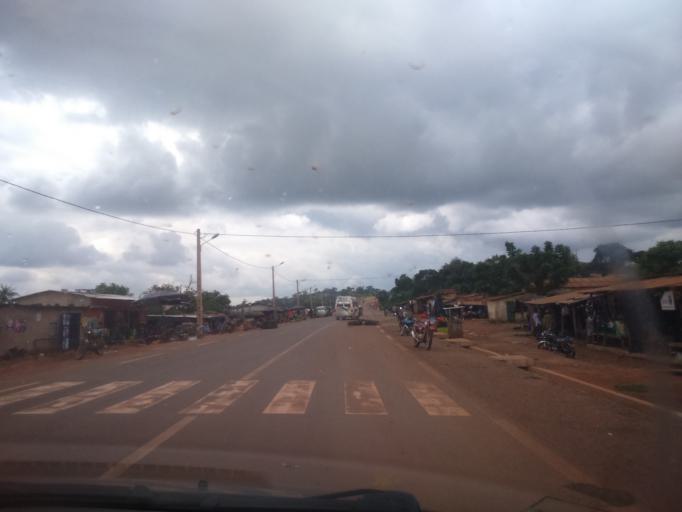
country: CI
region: Moyen-Comoe
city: Abengourou
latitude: 6.6395
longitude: -3.7142
